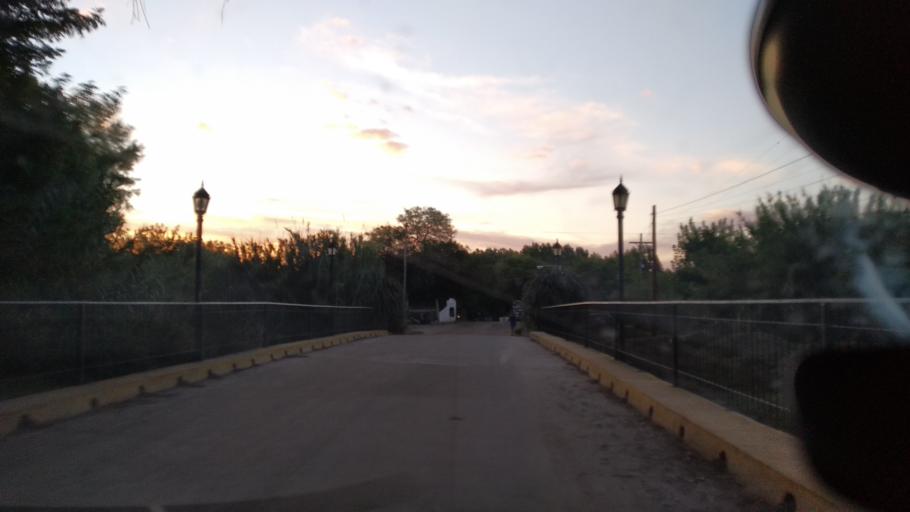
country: AR
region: Cordoba
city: Villa Las Rosas
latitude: -31.9440
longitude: -65.0669
